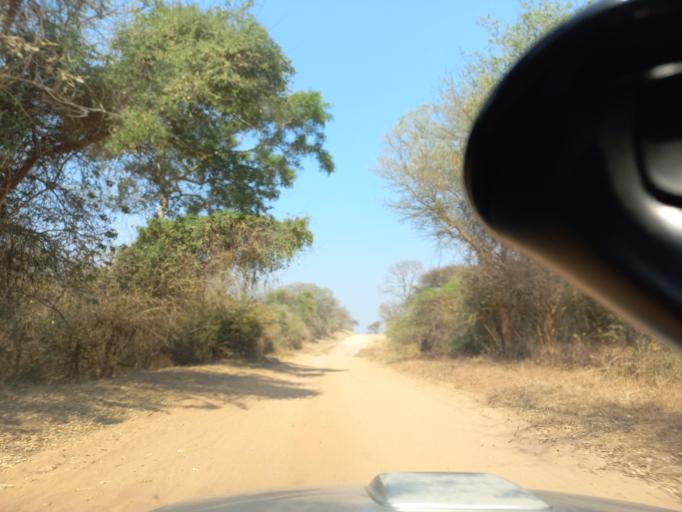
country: ZW
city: Chirundu
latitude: -15.9253
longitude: 28.8817
